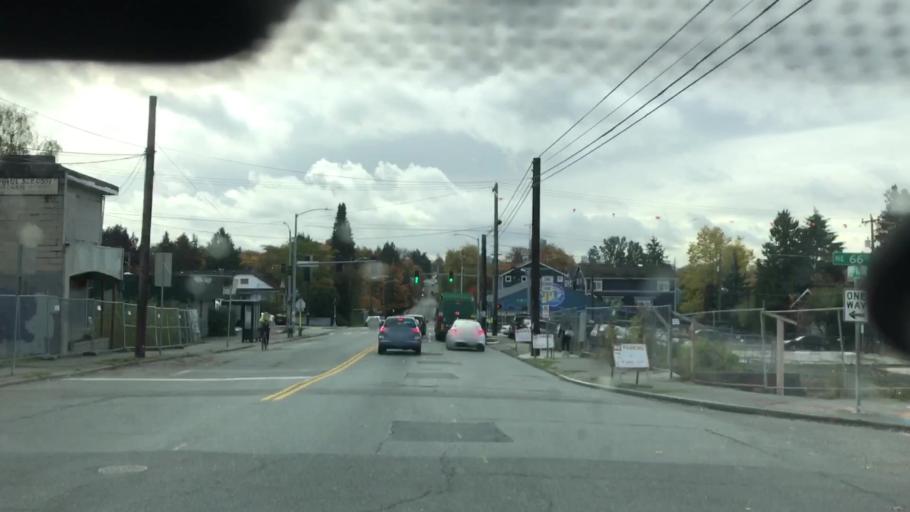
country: US
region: Washington
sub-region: King County
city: Seattle
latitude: 47.6766
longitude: -122.3120
